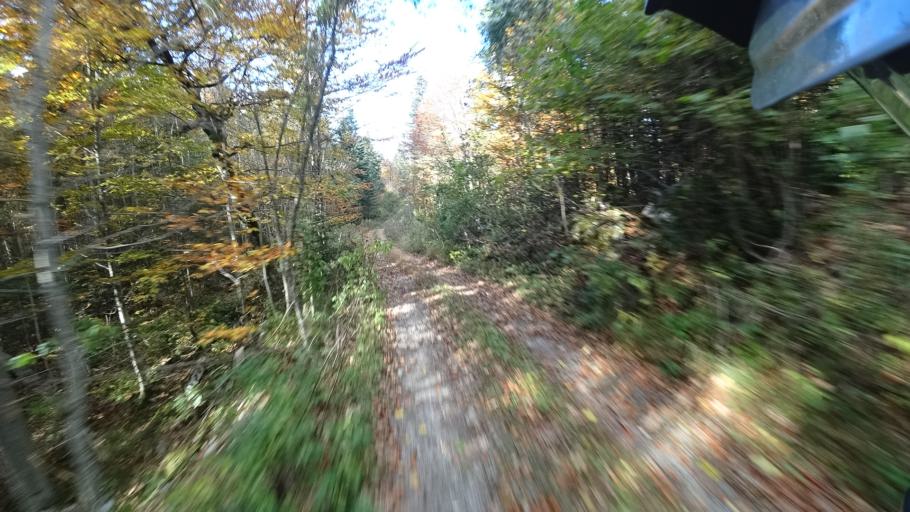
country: HR
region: Karlovacka
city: Plaski
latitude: 45.0542
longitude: 15.3327
